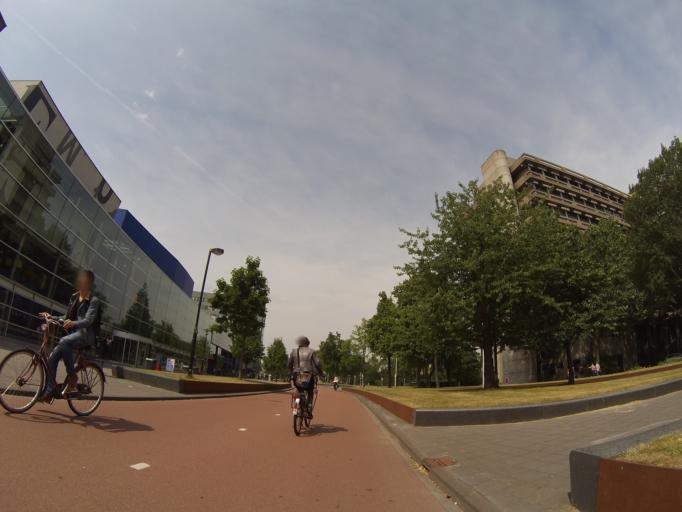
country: NL
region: Utrecht
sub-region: Gemeente De Bilt
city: De Bilt
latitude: 52.0847
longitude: 5.1699
